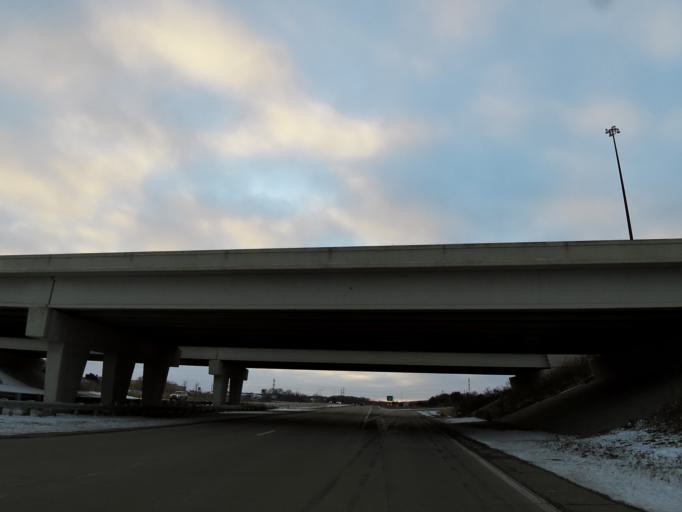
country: US
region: Minnesota
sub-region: Scott County
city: Prior Lake
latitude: 44.7840
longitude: -93.4125
